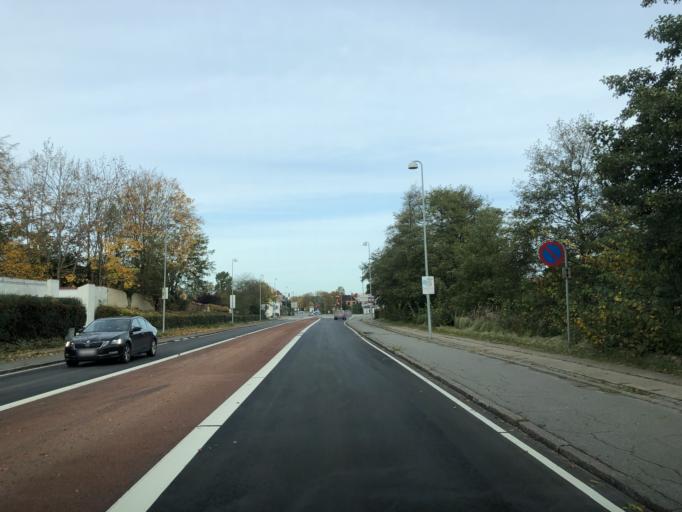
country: DK
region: Capital Region
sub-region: Hillerod Kommune
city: Hillerod
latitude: 55.9306
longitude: 12.3175
